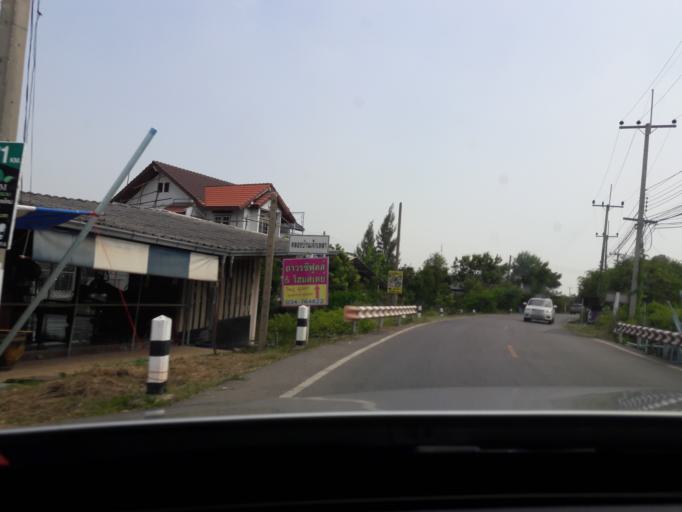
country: TH
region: Samut Songkhram
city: Amphawa
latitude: 13.3386
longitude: 99.9593
